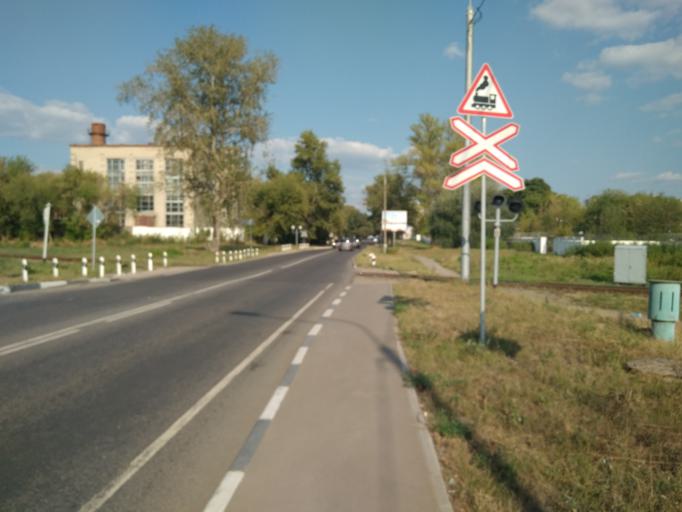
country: RU
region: Moskovskaya
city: Zhukovskiy
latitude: 55.5729
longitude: 38.1161
